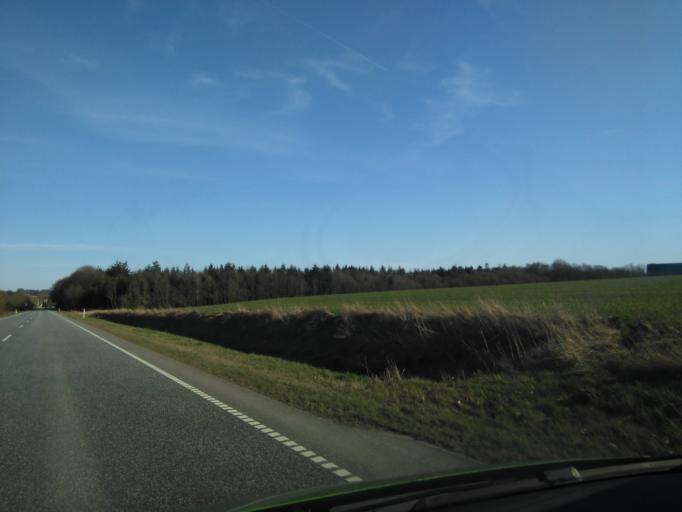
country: DK
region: Central Jutland
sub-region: Horsens Kommune
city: Braedstrup
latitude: 55.9047
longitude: 9.6005
